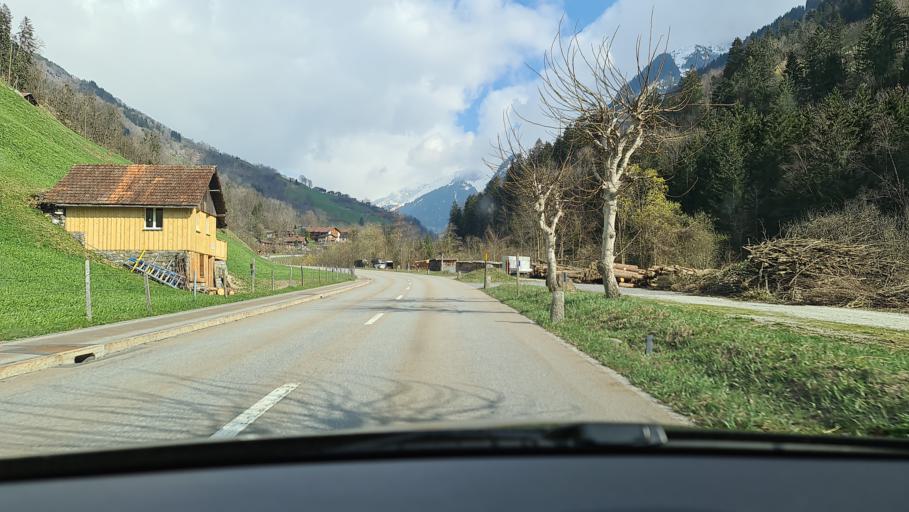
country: CH
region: Uri
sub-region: Uri
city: Burglen
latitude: 46.8788
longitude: 8.7016
